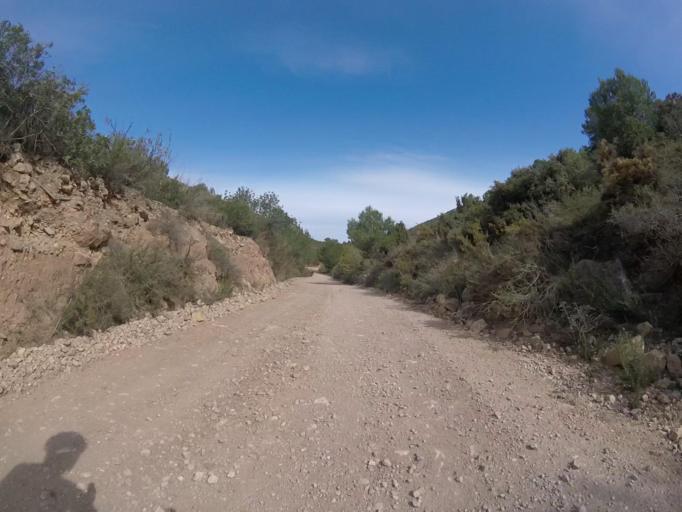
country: ES
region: Valencia
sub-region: Provincia de Castello
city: Torreblanca
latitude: 40.1988
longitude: 0.1546
